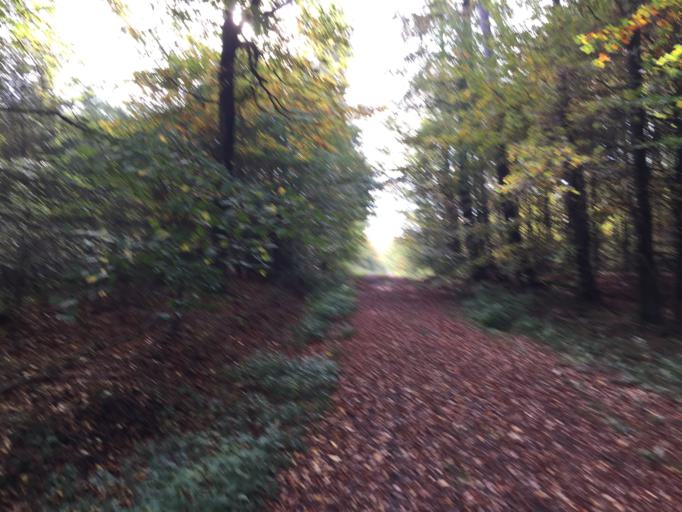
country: DE
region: Hesse
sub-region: Regierungsbezirk Giessen
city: Laubach
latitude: 50.5662
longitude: 8.9896
